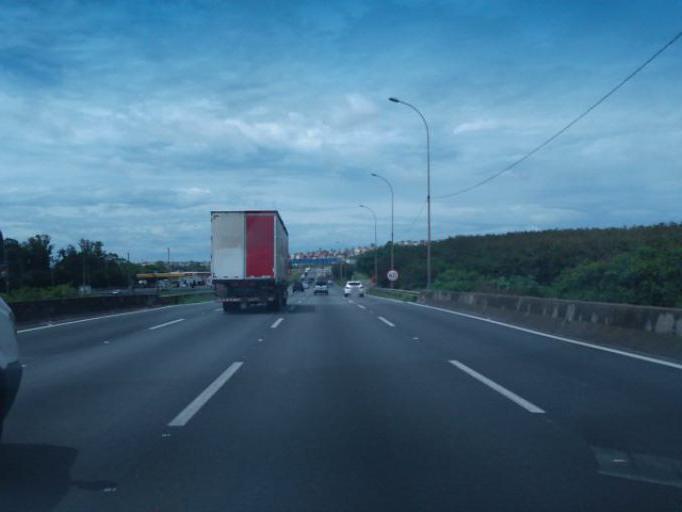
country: BR
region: Sao Paulo
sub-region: Carapicuiba
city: Carapicuiba
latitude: -23.5150
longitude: -46.8120
